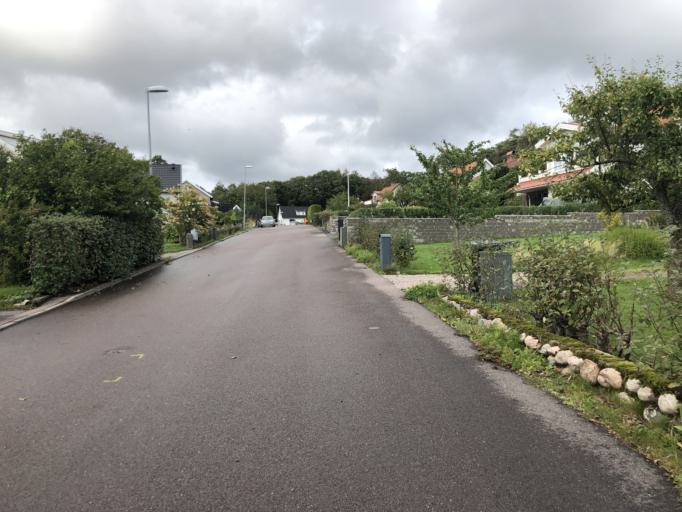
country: SE
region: Vaestra Goetaland
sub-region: Goteborg
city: Goeteborg
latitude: 57.7542
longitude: 11.9359
